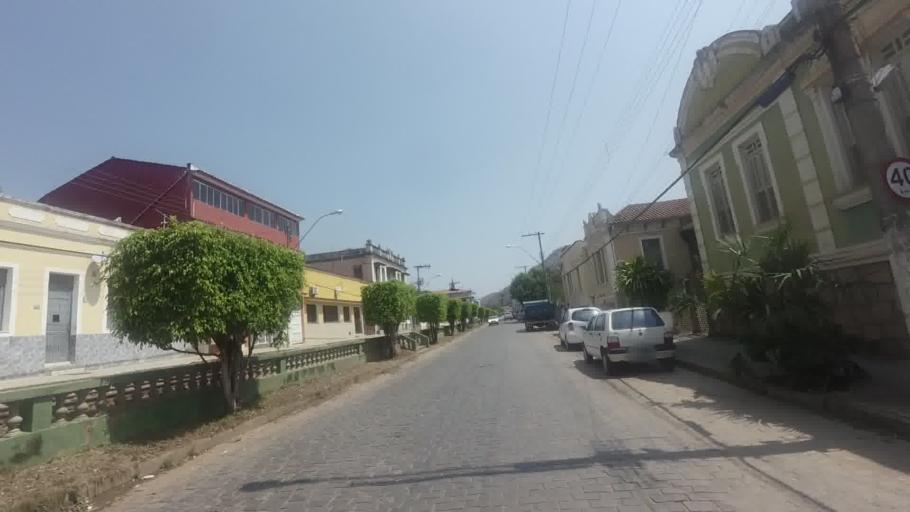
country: BR
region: Espirito Santo
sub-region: Mimoso Do Sul
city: Mimoso do Sul
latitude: -20.9496
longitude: -41.3428
